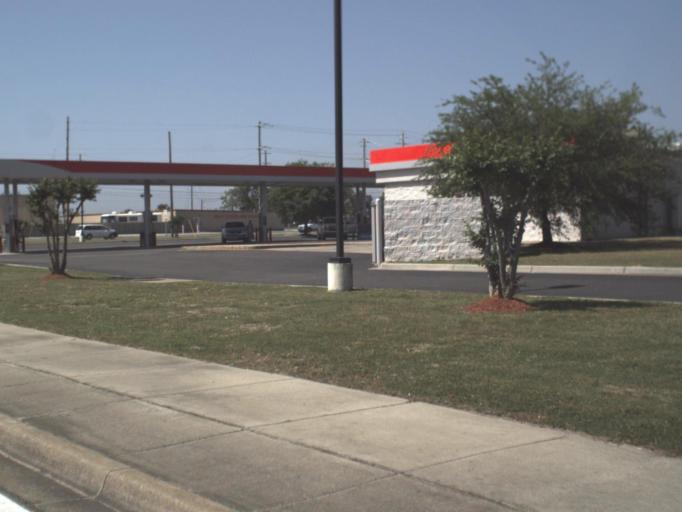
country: US
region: Florida
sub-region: Escambia County
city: Pensacola
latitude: 30.4129
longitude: -87.2417
